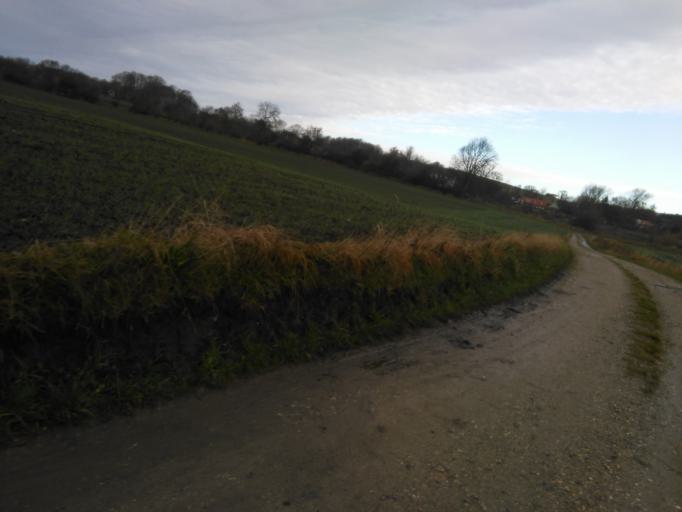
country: DK
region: Central Jutland
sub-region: Arhus Kommune
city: Marslet
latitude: 56.0803
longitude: 10.1825
